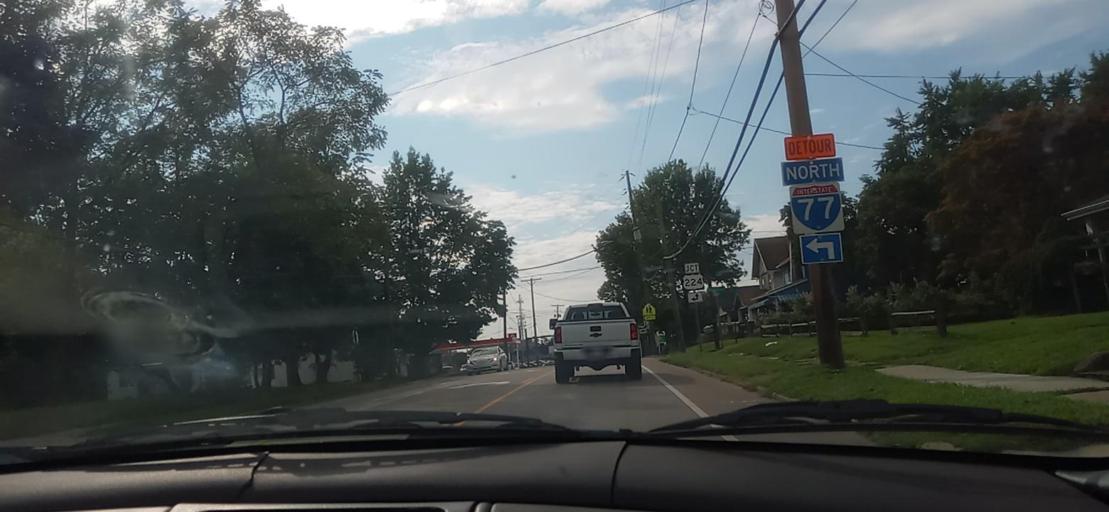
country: US
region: Ohio
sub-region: Summit County
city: Portage Lakes
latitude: 41.0302
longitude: -81.5446
